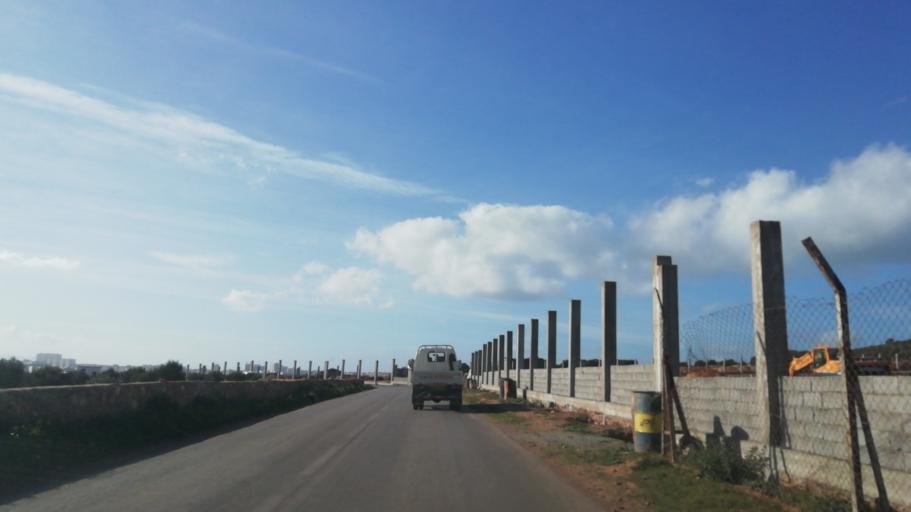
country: DZ
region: Oran
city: Bir el Djir
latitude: 35.7525
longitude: -0.5138
